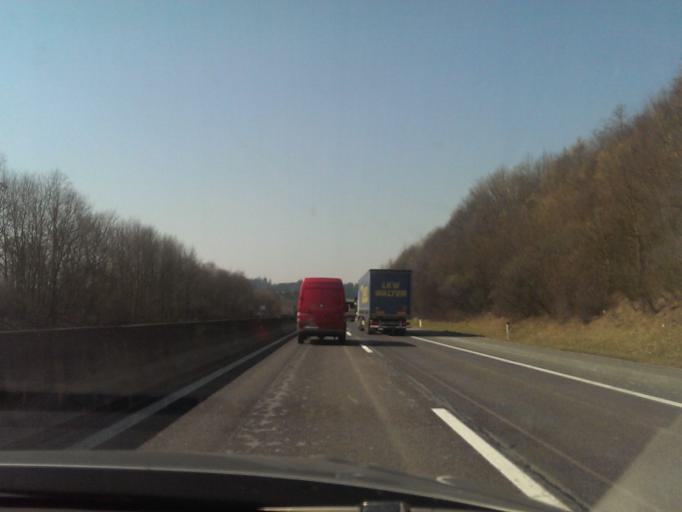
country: AT
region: Upper Austria
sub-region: Politischer Bezirk Ried im Innkreis
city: Ried im Innkreis
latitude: 48.2430
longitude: 13.5390
